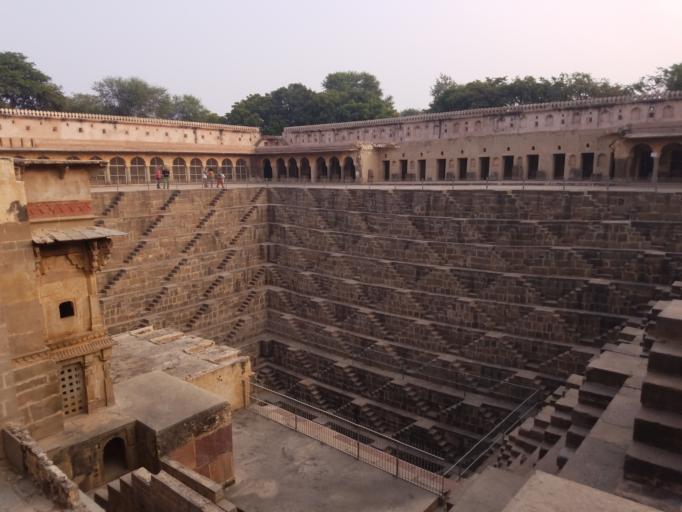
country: IN
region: Rajasthan
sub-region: Dausa
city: Abhaneri
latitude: 27.0074
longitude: 76.6063
